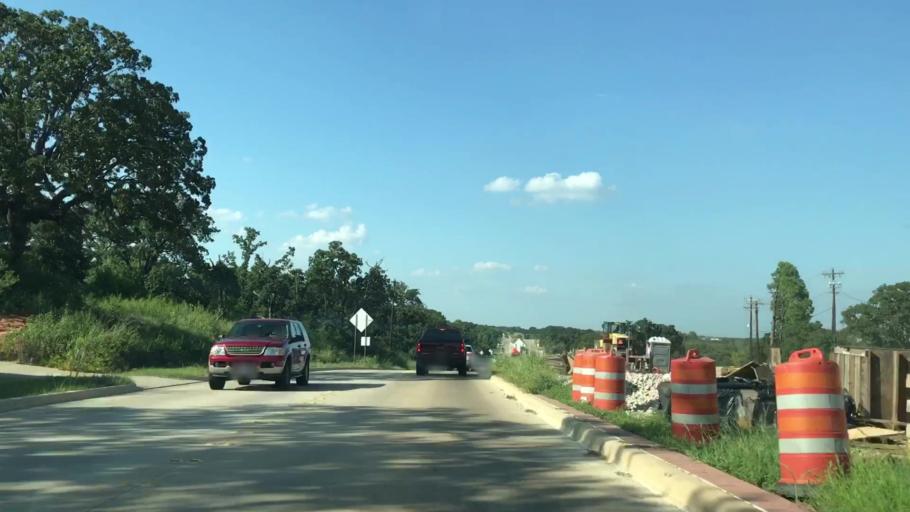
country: US
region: Texas
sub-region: Denton County
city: Trophy Club
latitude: 32.9591
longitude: -97.1860
